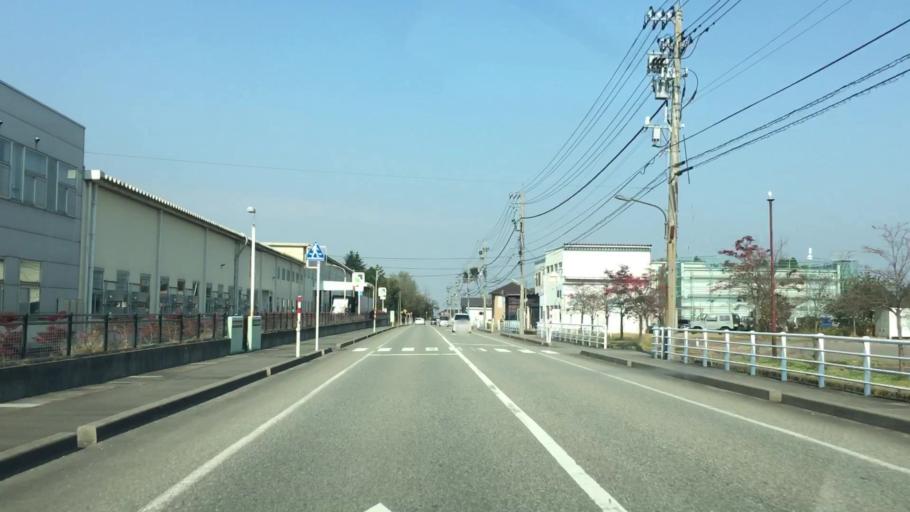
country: JP
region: Toyama
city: Yatsuomachi-higashikumisaka
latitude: 36.5877
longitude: 137.1910
